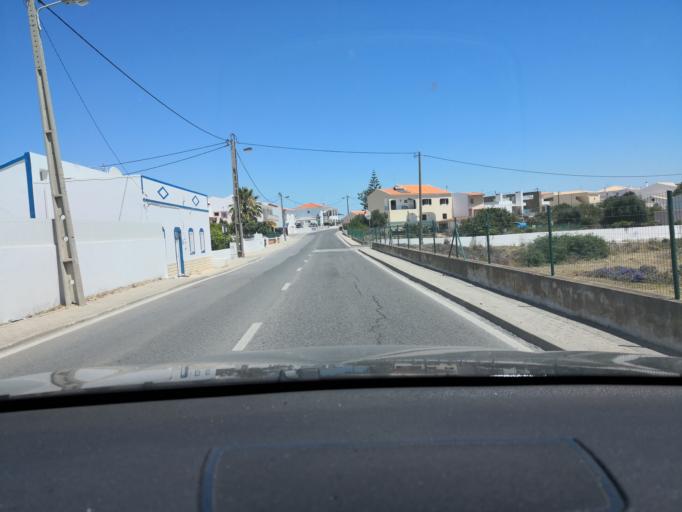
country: PT
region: Faro
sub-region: Albufeira
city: Ferreiras
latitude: 37.1058
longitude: -8.2142
